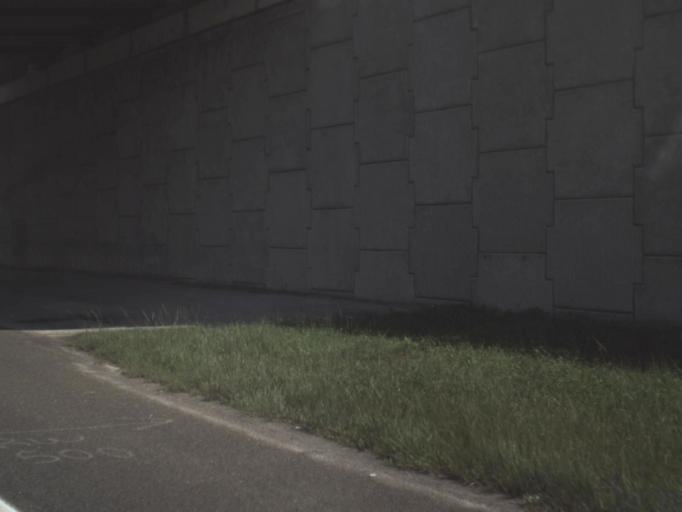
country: US
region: Florida
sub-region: Polk County
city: Fussels Corner
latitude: 28.0537
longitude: -81.8350
